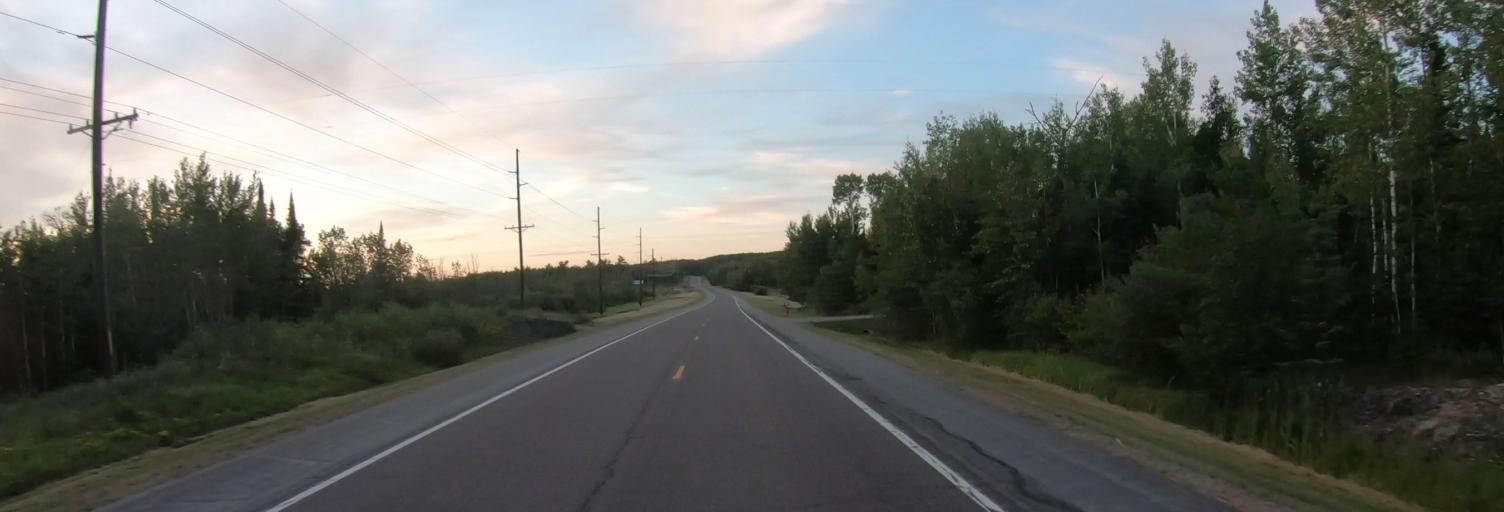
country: US
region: Minnesota
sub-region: Saint Louis County
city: Aurora
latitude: 47.8293
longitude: -92.3726
